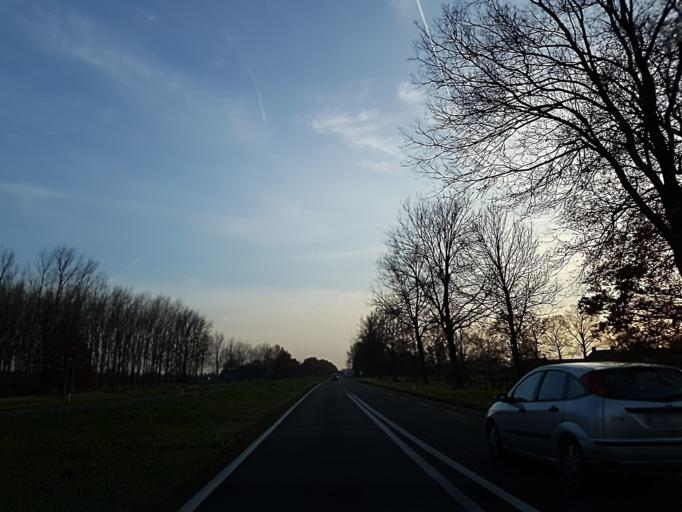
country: NL
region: North Brabant
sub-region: Roosendaal
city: Roosendaal
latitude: 51.5105
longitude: 4.4668
